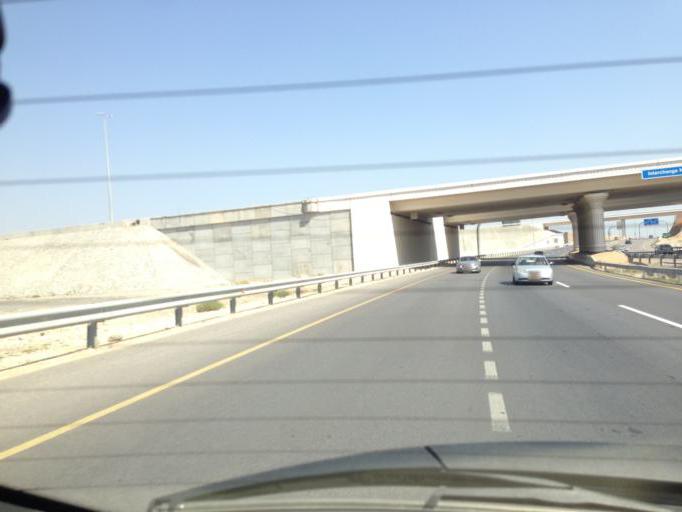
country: OM
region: Muhafazat Masqat
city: As Sib al Jadidah
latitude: 23.5658
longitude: 58.1892
